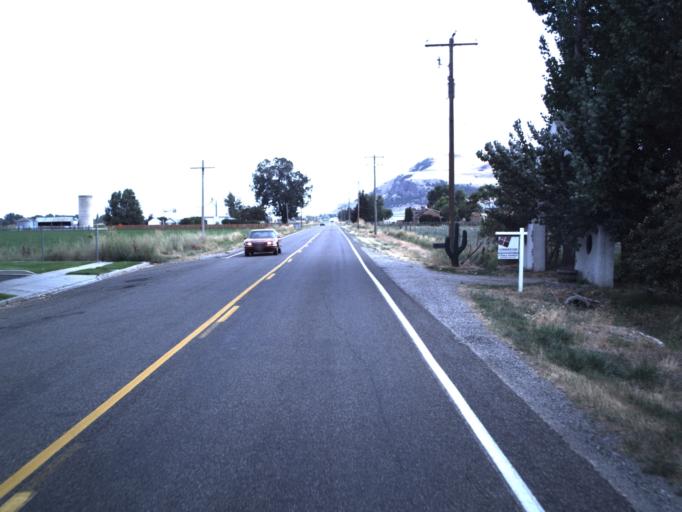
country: US
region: Utah
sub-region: Cache County
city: Lewiston
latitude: 41.9383
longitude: -111.9536
